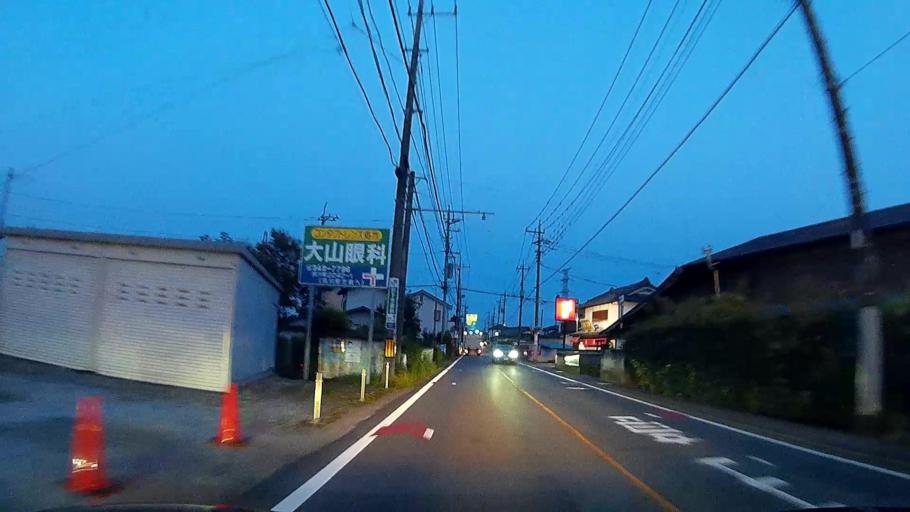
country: JP
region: Gunma
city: Takasaki
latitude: 36.3443
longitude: 138.9634
